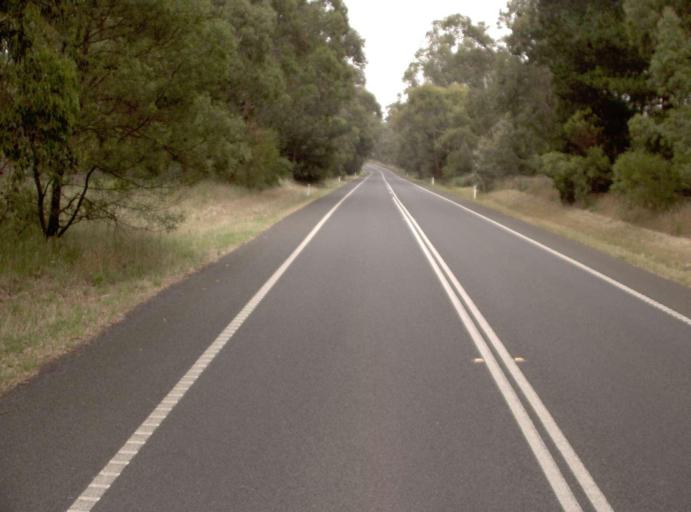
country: AU
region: Victoria
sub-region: Latrobe
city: Morwell
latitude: -38.2869
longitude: 146.3119
